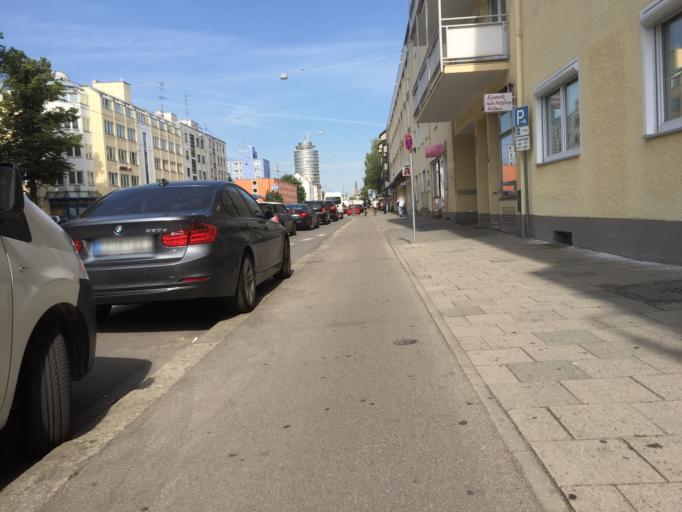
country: DE
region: Bavaria
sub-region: Upper Bavaria
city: Bogenhausen
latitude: 48.1304
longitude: 11.6195
